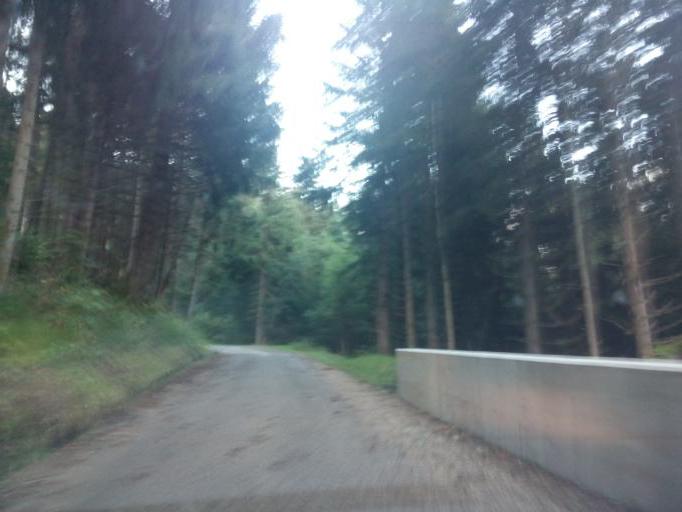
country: FR
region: Rhone-Alpes
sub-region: Departement de l'Isere
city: Le Champ-pres-Froges
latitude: 45.2395
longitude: 5.9833
